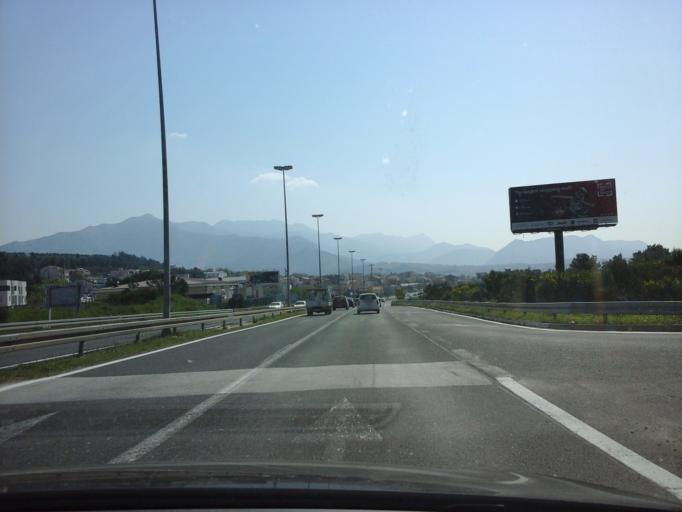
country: HR
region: Splitsko-Dalmatinska
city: Vranjic
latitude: 43.5447
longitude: 16.4563
